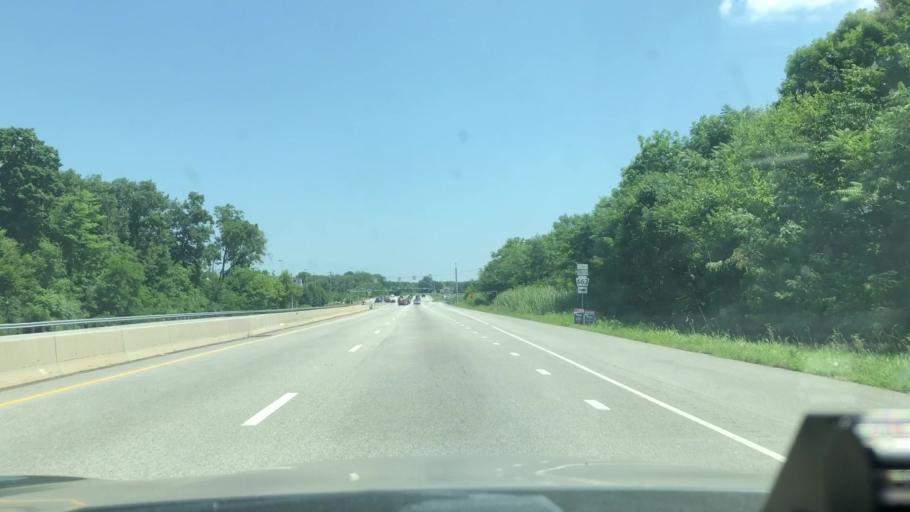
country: US
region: Pennsylvania
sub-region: Montgomery County
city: Pottstown
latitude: 40.2622
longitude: -75.6522
